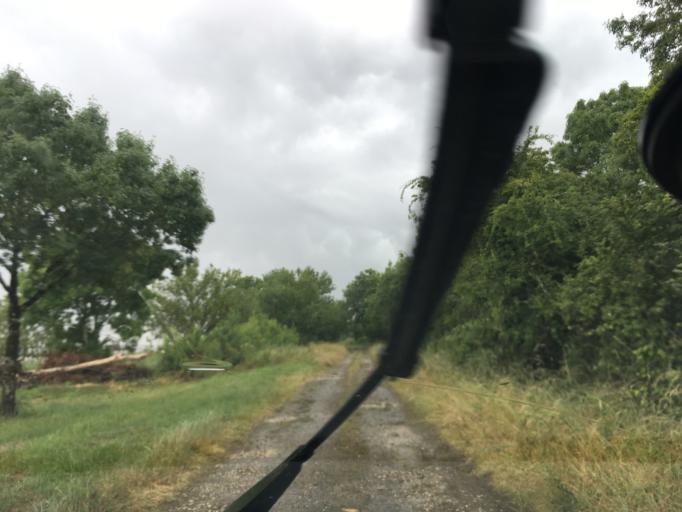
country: FR
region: Aquitaine
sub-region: Departement de la Gironde
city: Saint-Estephe
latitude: 45.3340
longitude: -0.7971
